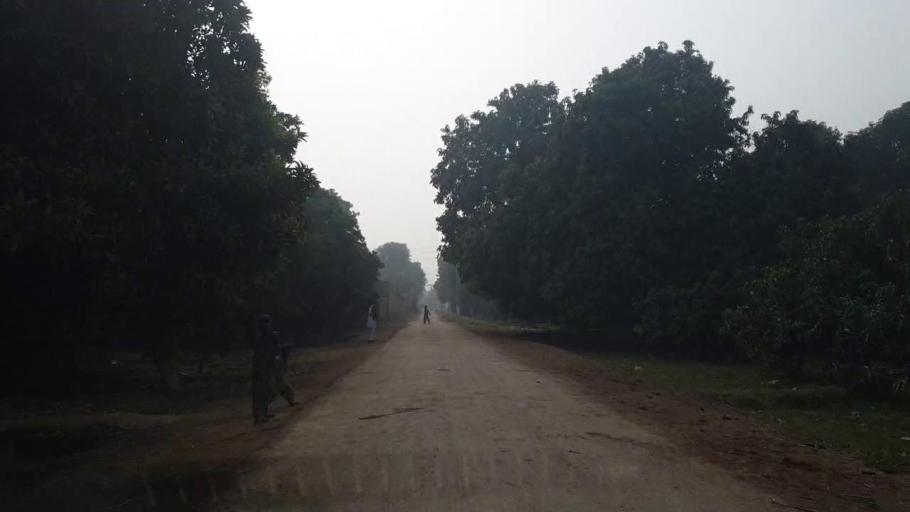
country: PK
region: Sindh
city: Tando Adam
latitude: 25.7850
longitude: 68.5962
